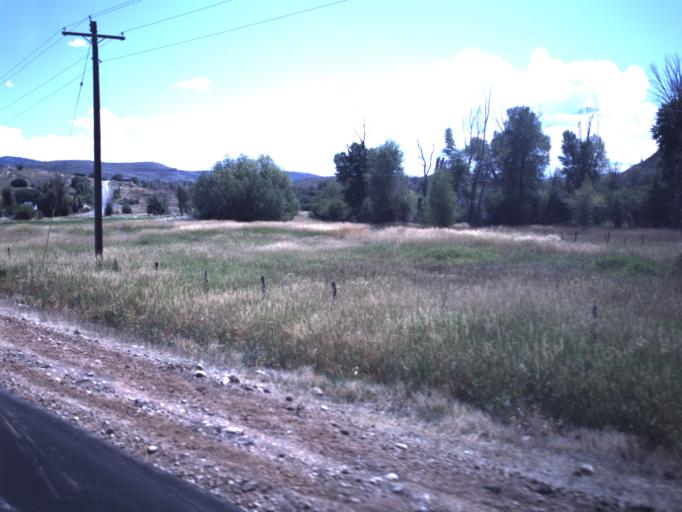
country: US
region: Utah
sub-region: Summit County
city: Francis
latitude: 40.6117
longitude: -111.3011
